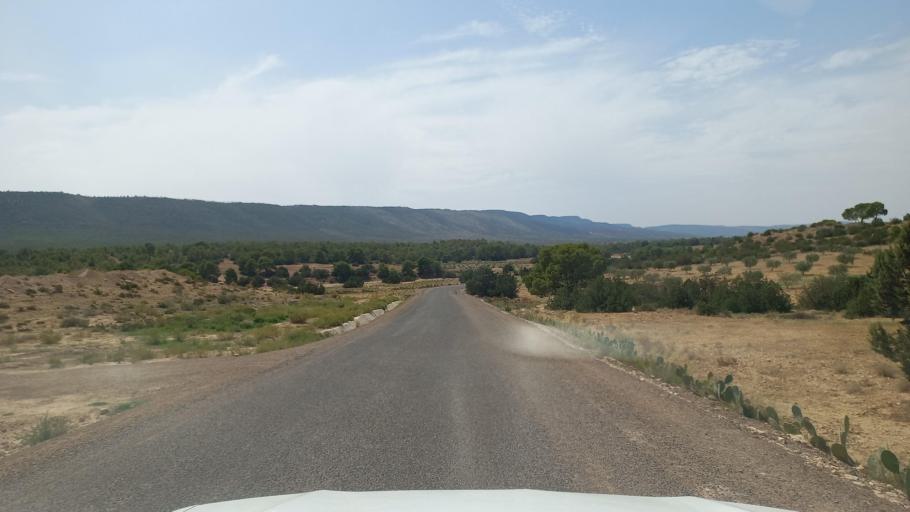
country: TN
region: Al Qasrayn
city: Sbiba
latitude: 35.3882
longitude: 8.9463
